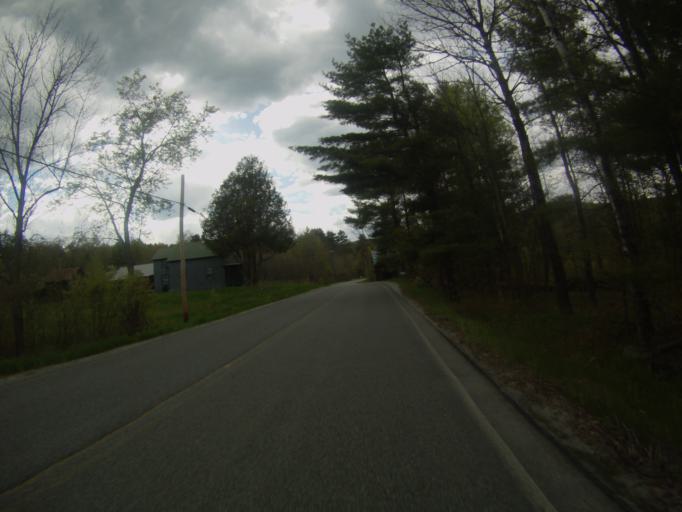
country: US
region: New York
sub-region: Essex County
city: Mineville
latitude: 44.0522
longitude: -73.5434
